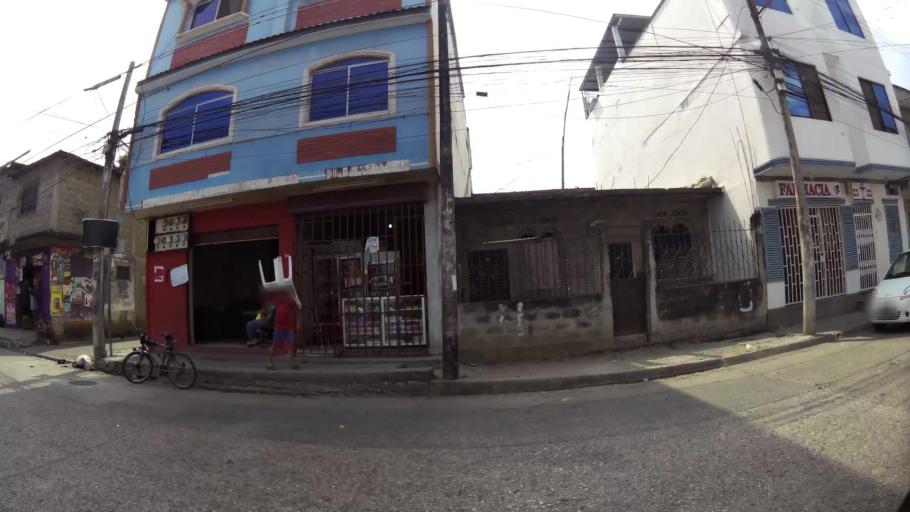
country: EC
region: Guayas
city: Santa Lucia
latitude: -2.1315
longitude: -79.9392
